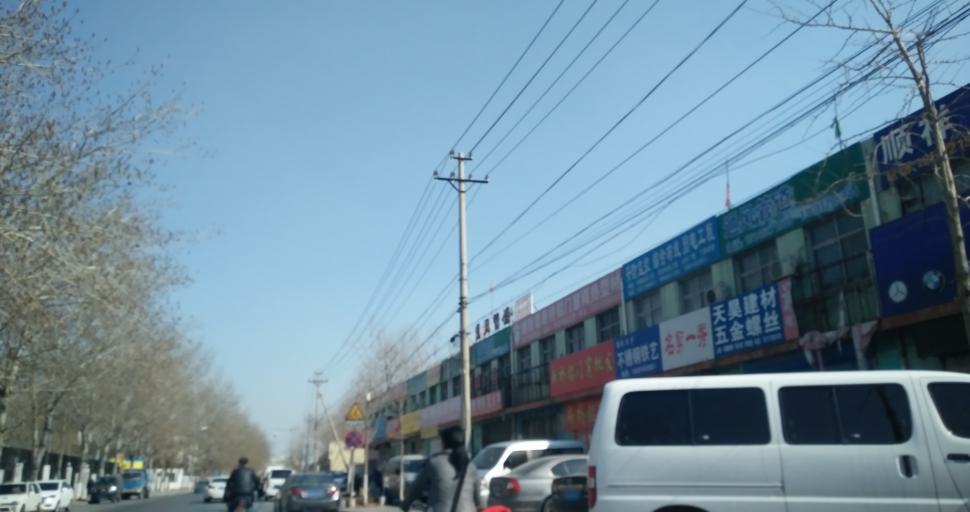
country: CN
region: Beijing
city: Jiugong
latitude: 39.8084
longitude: 116.4452
